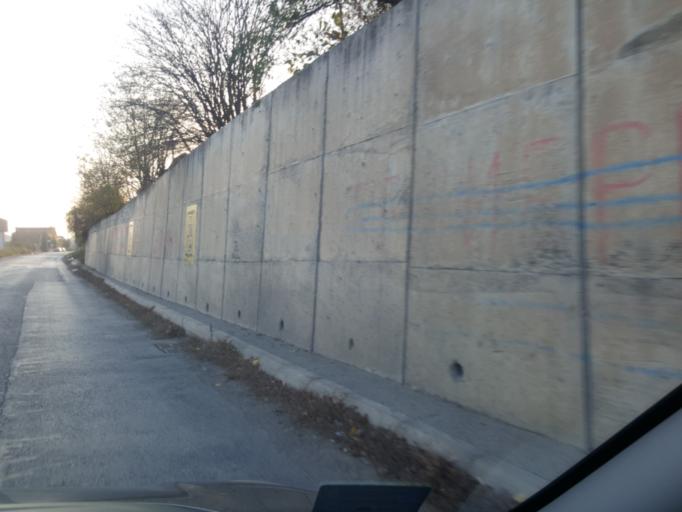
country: RS
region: Central Serbia
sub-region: Zajecarski Okrug
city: Zajecar
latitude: 43.9182
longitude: 22.2891
